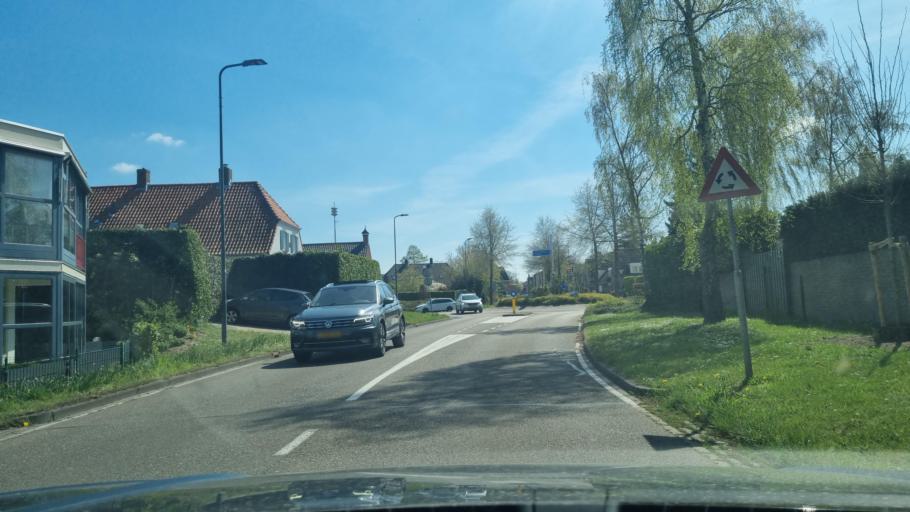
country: NL
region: North Brabant
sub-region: Gemeente 's-Hertogenbosch
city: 's-Hertogenbosch
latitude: 51.7205
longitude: 5.3643
